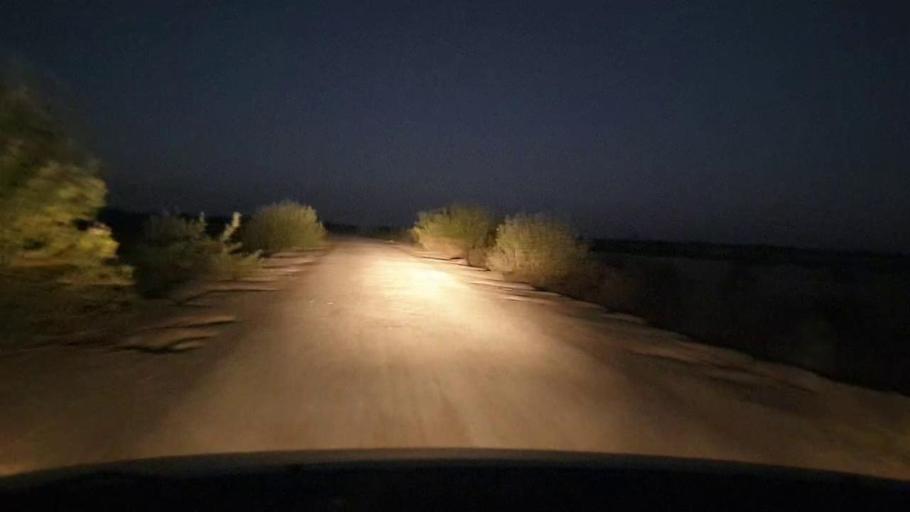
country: PK
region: Sindh
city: Phulji
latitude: 26.9190
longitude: 67.4822
